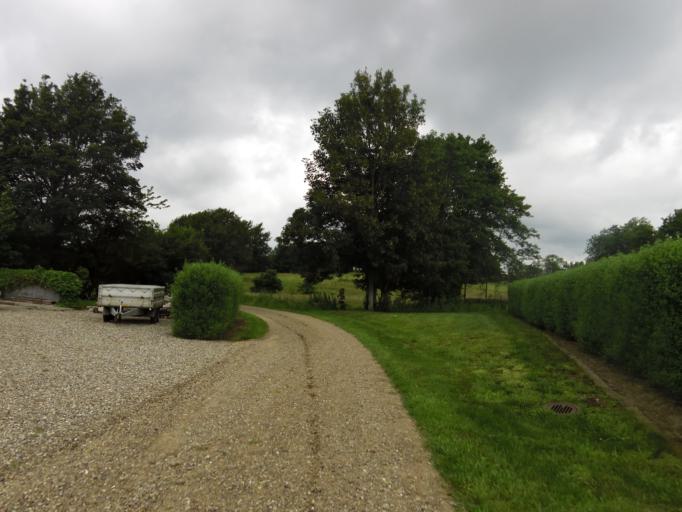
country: DK
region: South Denmark
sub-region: Tonder Kommune
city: Toftlund
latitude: 55.1230
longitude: 9.0741
